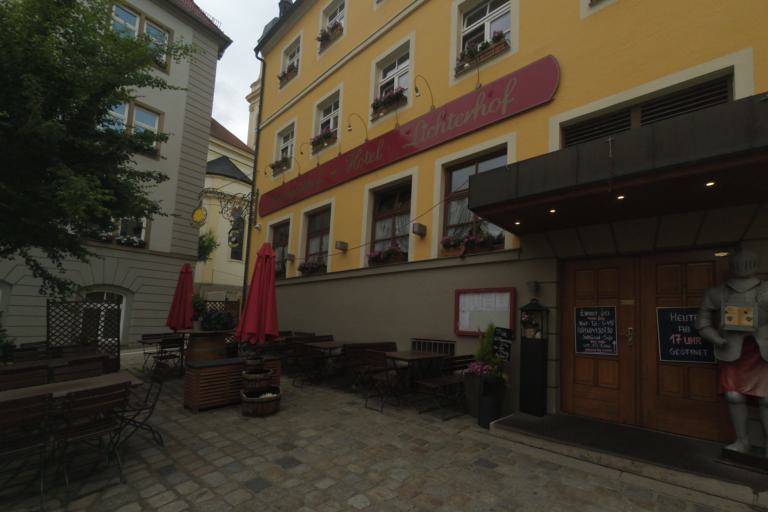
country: DE
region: Bavaria
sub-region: Regierungsbezirk Mittelfranken
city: Uffenheim
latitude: 49.5456
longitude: 10.2296
